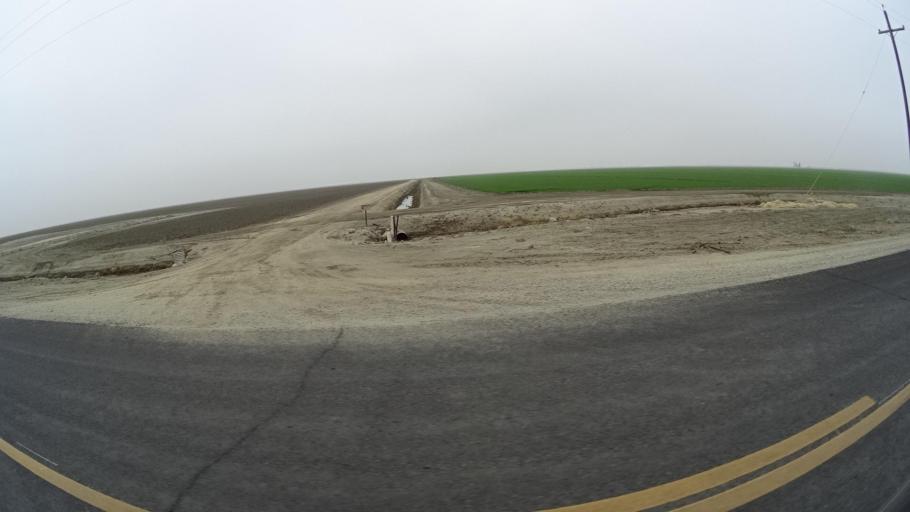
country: US
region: California
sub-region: Kern County
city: Greenfield
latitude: 35.1804
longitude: -119.1906
